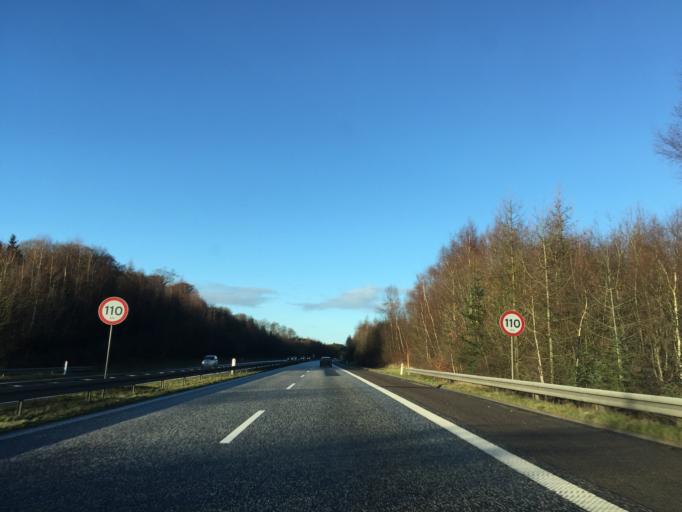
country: DK
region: South Denmark
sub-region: Fredericia Kommune
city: Taulov
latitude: 55.5589
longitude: 9.6274
